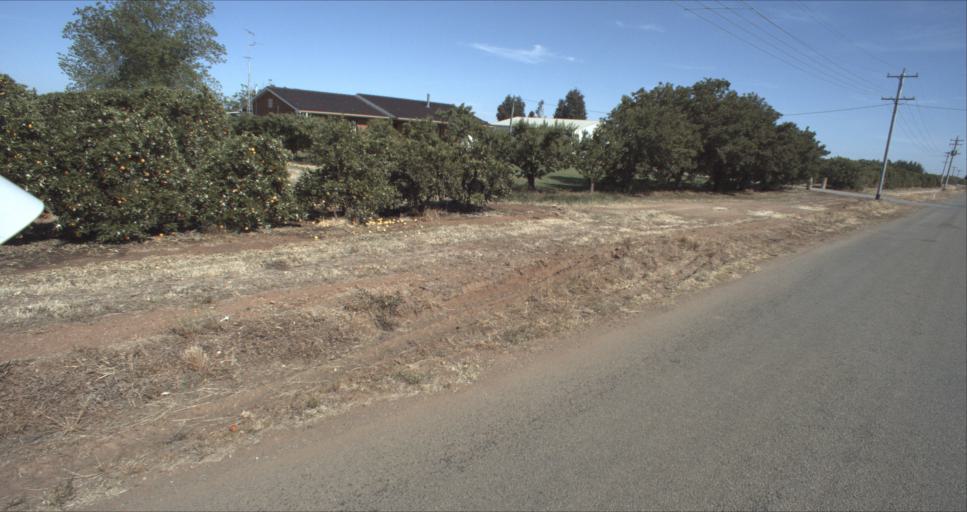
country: AU
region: New South Wales
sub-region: Leeton
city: Leeton
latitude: -34.5746
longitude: 146.4763
